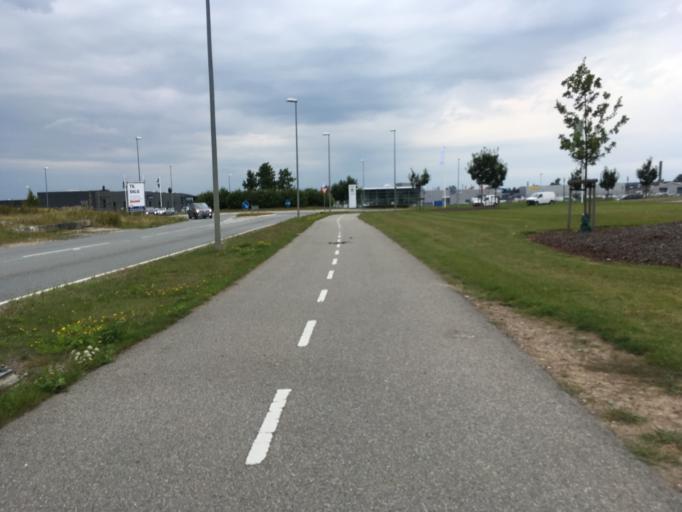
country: DK
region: Capital Region
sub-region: Hillerod Kommune
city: Hillerod
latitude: 55.9267
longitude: 12.2633
